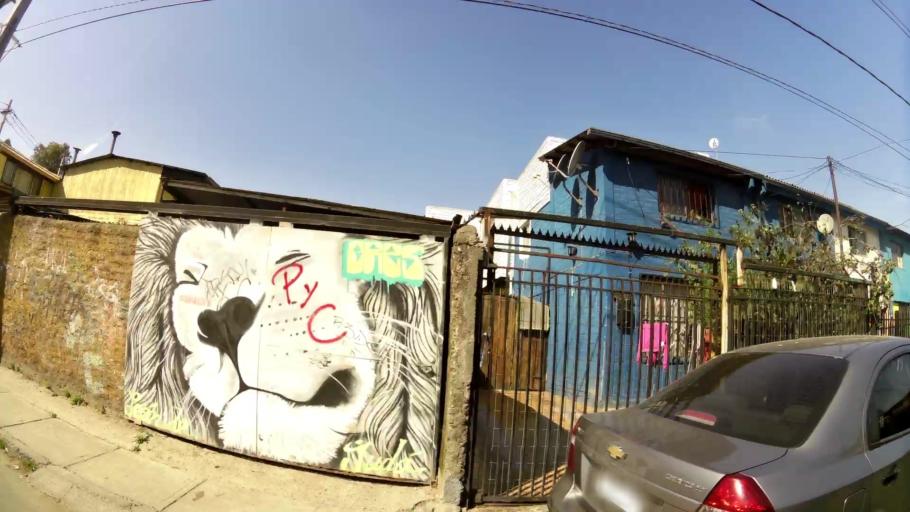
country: CL
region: Santiago Metropolitan
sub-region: Provincia de Santiago
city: La Pintana
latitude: -33.5614
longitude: -70.6285
